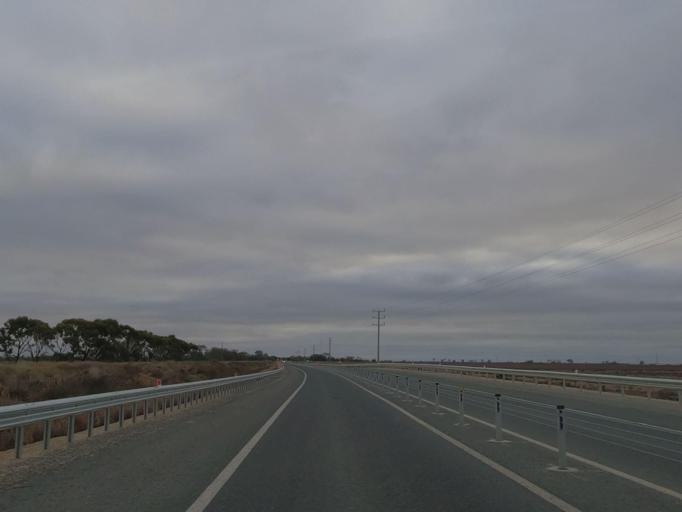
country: AU
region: Victoria
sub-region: Swan Hill
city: Swan Hill
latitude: -35.5439
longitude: 143.7576
